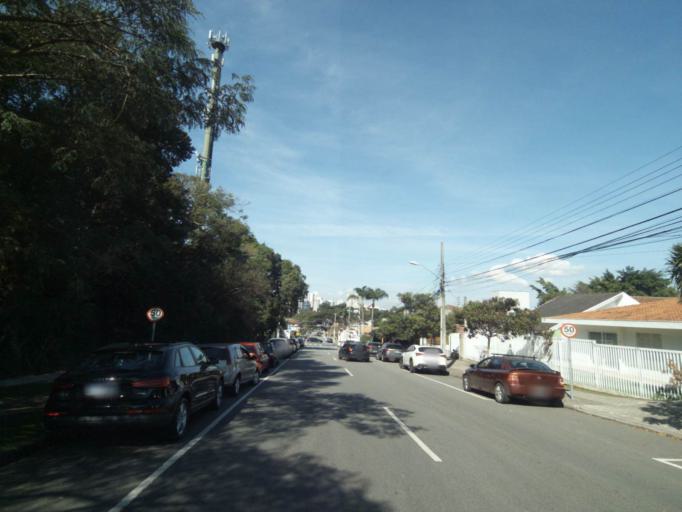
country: BR
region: Parana
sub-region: Curitiba
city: Curitiba
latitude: -25.4384
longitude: -49.2961
